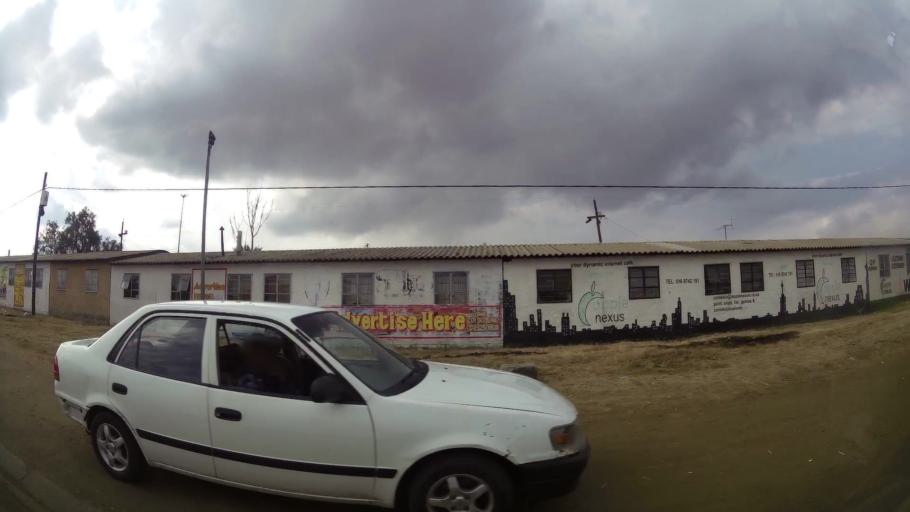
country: ZA
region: Orange Free State
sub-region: Fezile Dabi District Municipality
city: Sasolburg
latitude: -26.8424
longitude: 27.8527
